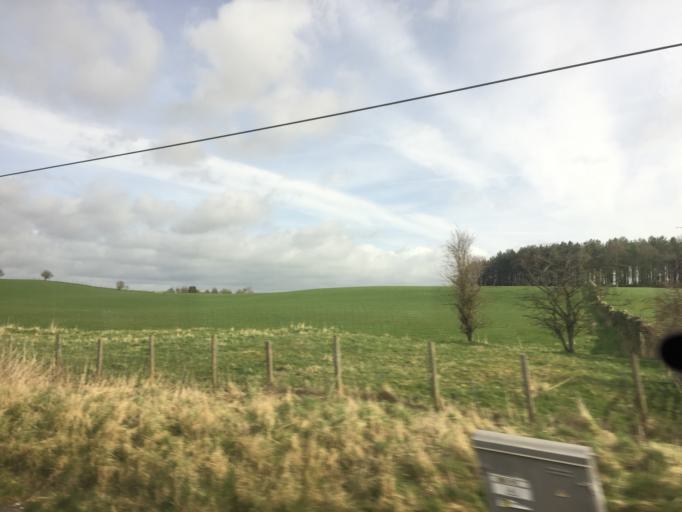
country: GB
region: England
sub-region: Cumbria
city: Penrith
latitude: 54.7402
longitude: -2.8059
